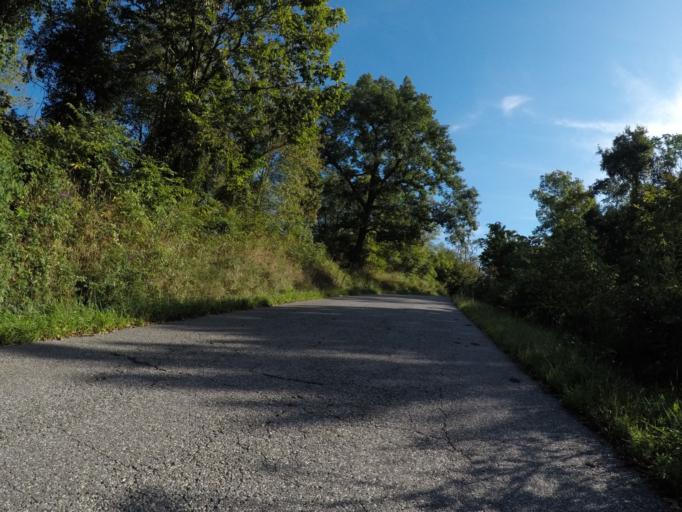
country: US
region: Ohio
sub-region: Lawrence County
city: Burlington
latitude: 38.5256
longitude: -82.5267
